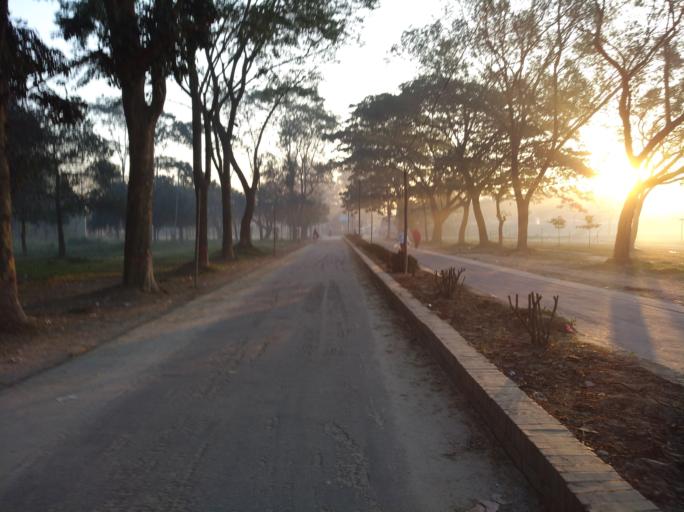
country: BD
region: Dhaka
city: Tungi
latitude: 23.8799
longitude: 90.2713
